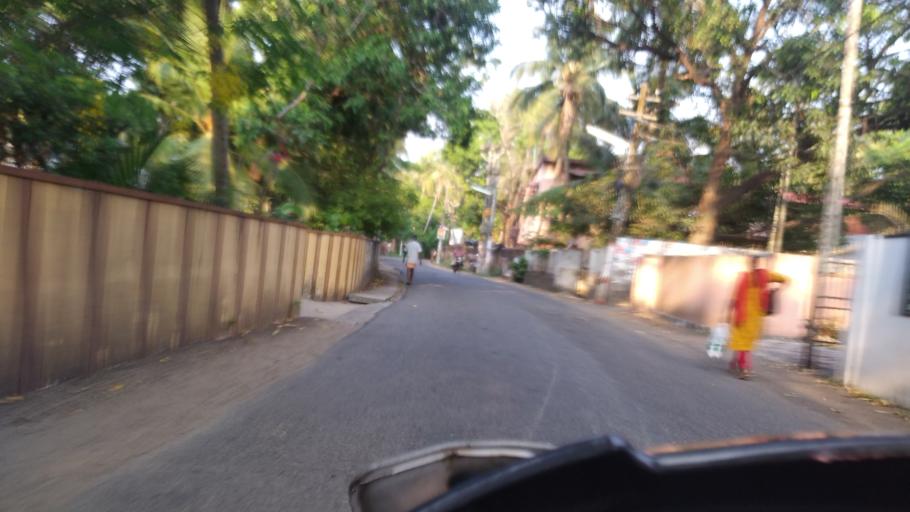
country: IN
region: Kerala
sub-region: Thrissur District
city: Thanniyam
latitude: 10.4384
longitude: 76.0857
